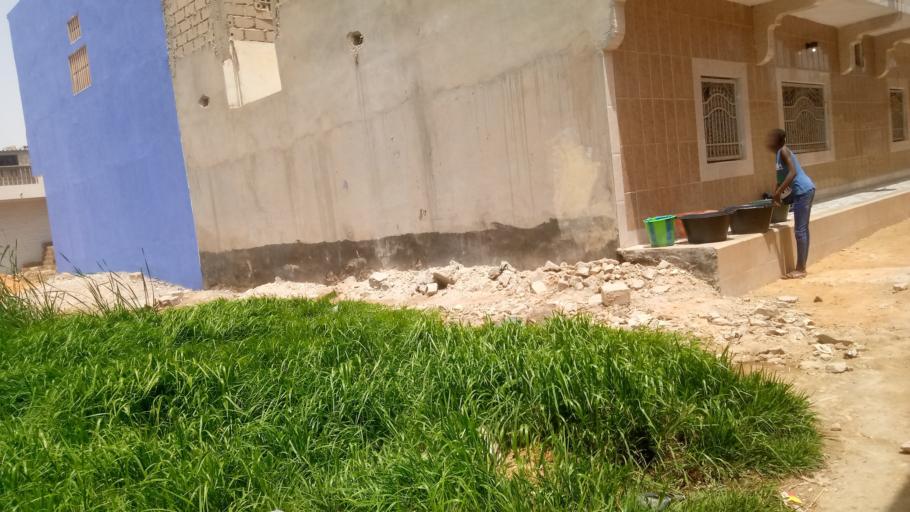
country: SN
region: Saint-Louis
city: Saint-Louis
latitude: 16.0160
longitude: -16.4844
